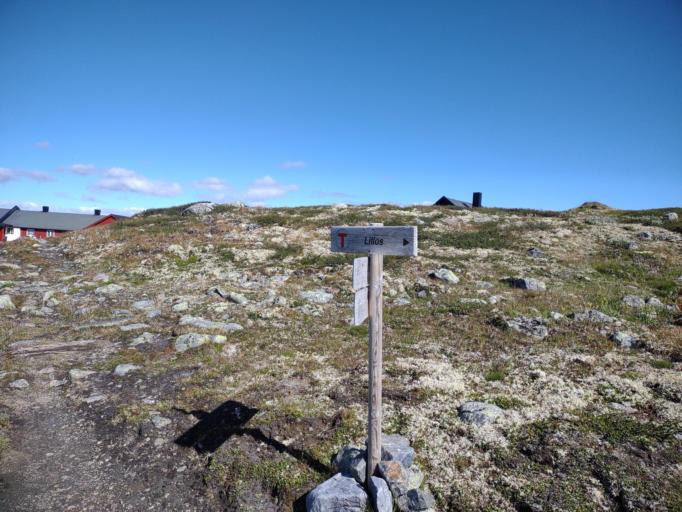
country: NO
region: Hordaland
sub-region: Eidfjord
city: Eidfjord
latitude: 60.1826
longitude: 7.4015
